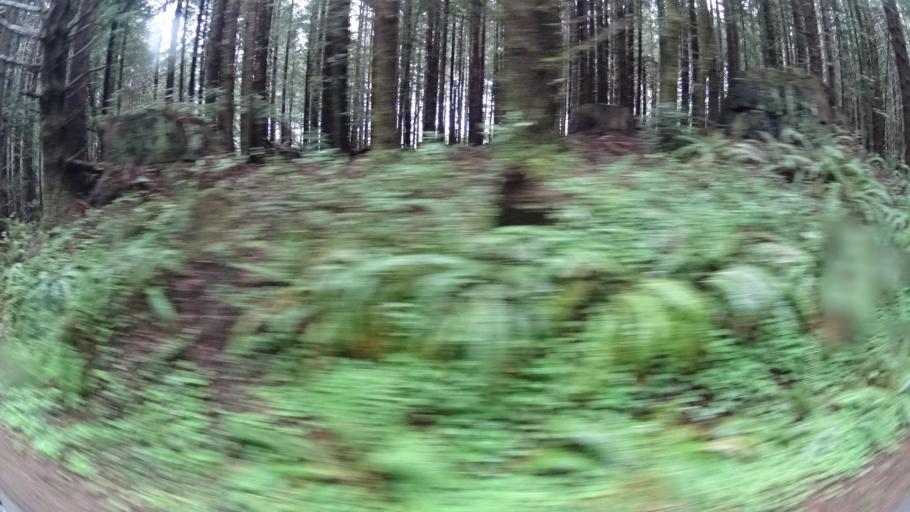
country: US
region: California
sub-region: Humboldt County
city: Westhaven-Moonstone
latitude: 41.2422
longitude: -123.9825
